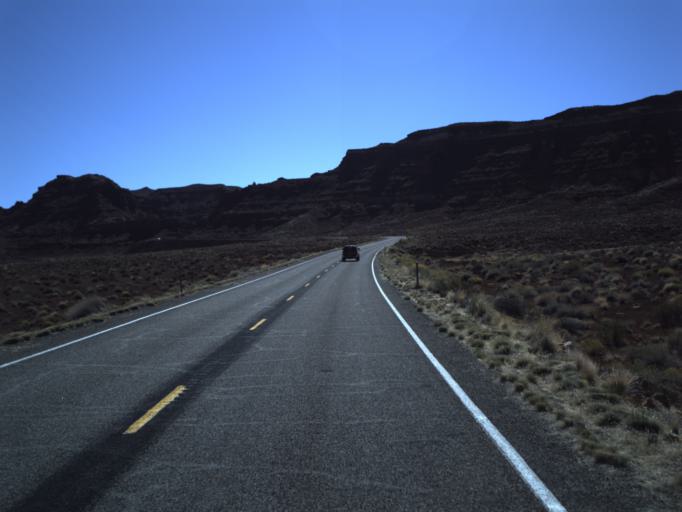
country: US
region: Utah
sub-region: San Juan County
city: Blanding
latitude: 37.8769
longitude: -110.3504
